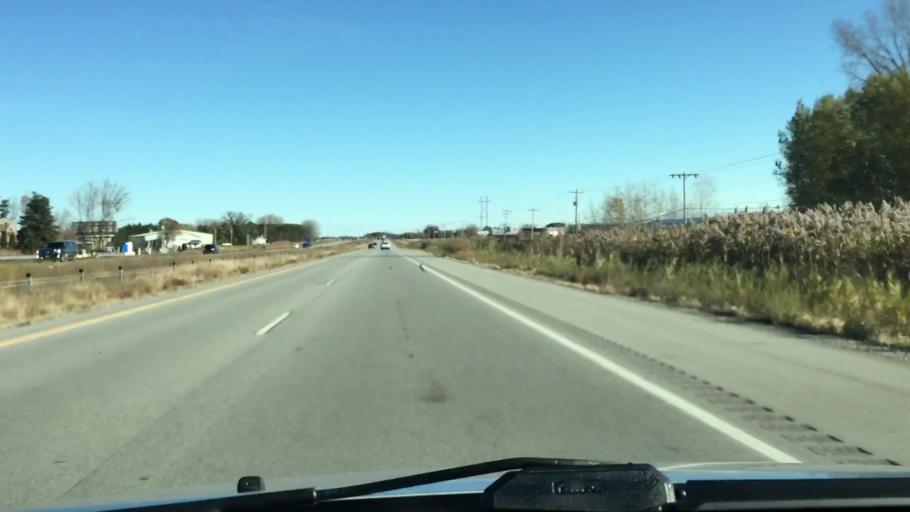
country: US
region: Wisconsin
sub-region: Brown County
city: Wrightstown
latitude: 44.3720
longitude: -88.1728
